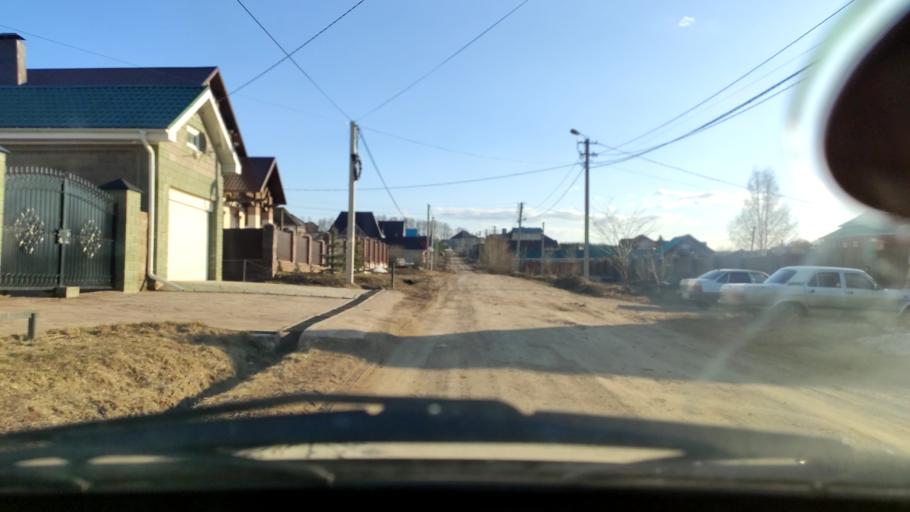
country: RU
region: Bashkortostan
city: Kabakovo
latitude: 54.6345
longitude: 56.0677
